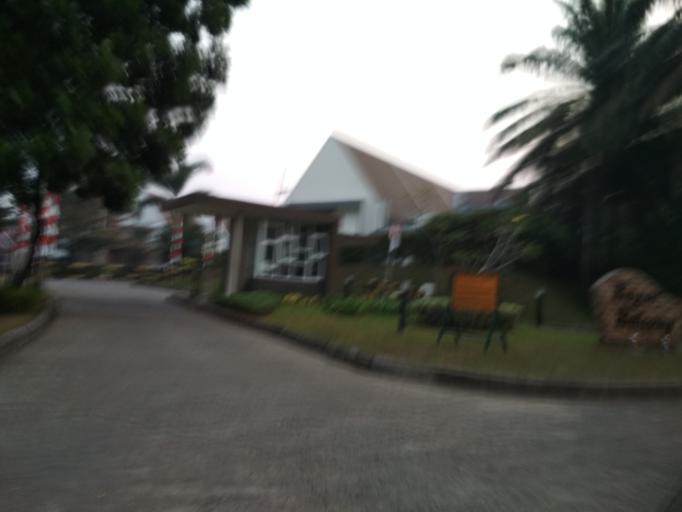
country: ID
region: West Java
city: Caringin
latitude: -6.6626
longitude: 106.8430
